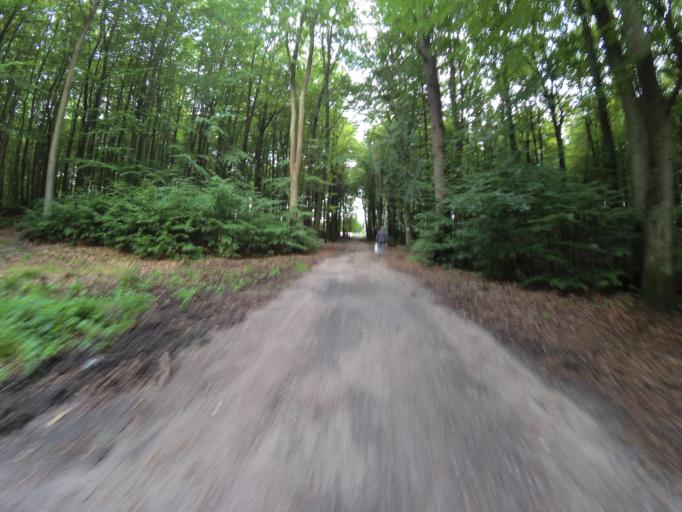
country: PL
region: Pomeranian Voivodeship
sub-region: Gdynia
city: Wielki Kack
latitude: 54.5009
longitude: 18.4942
